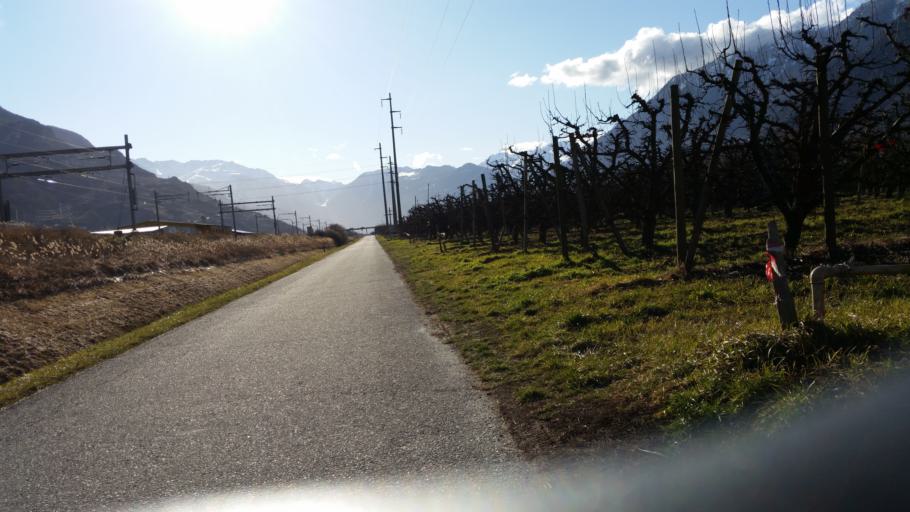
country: CH
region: Valais
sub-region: Martigny District
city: Saillon
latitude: 46.1630
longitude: 7.2011
